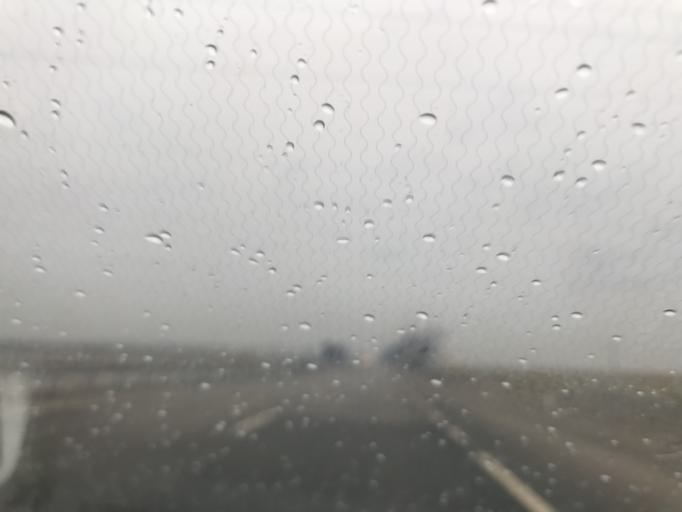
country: RU
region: Krasnodarskiy
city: Pavlovskaya
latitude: 46.1431
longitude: 39.8525
